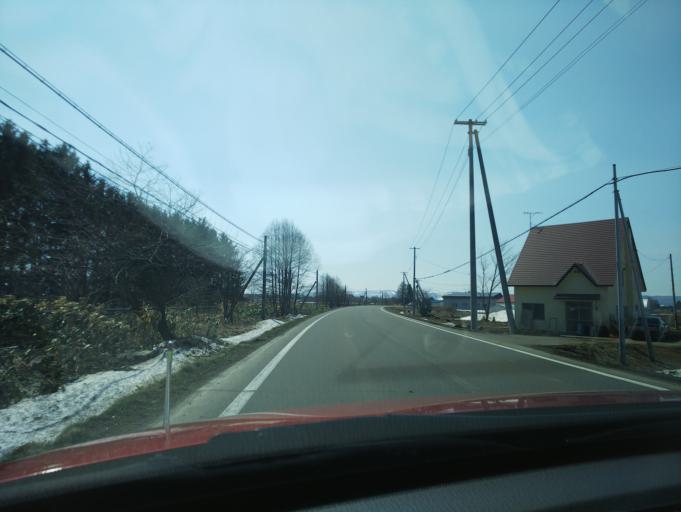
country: JP
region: Hokkaido
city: Nayoro
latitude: 44.3171
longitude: 142.4632
